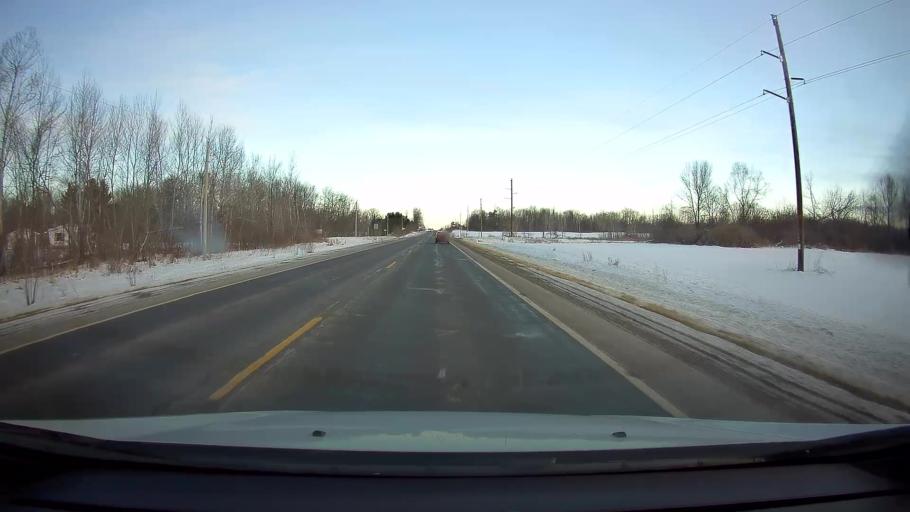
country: US
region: Wisconsin
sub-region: Barron County
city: Turtle Lake
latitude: 45.3585
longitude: -92.1668
